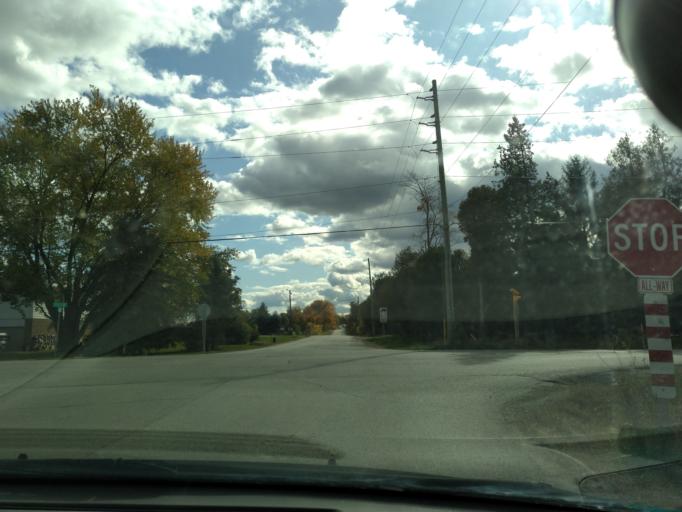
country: CA
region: Ontario
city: Bradford West Gwillimbury
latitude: 44.0818
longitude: -79.5958
